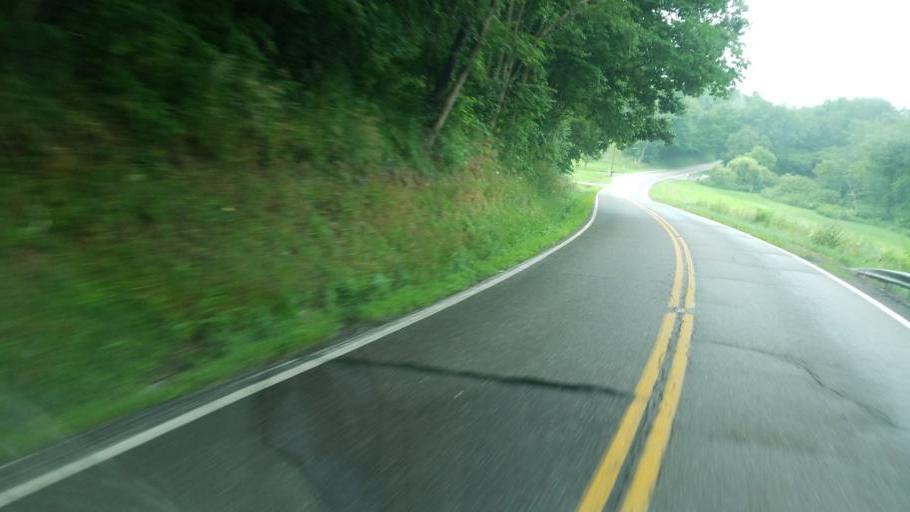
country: US
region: Ohio
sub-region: Carroll County
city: Carrollton
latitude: 40.4640
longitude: -80.9909
